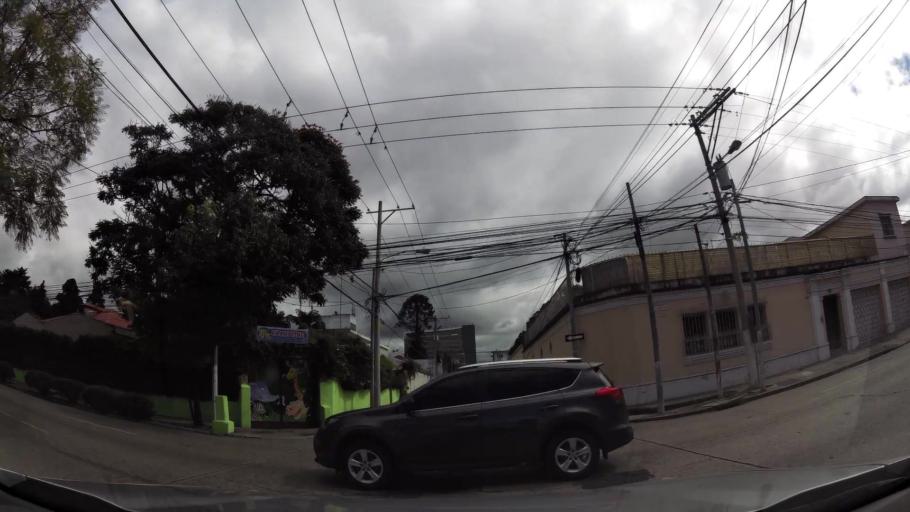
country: GT
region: Guatemala
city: Guatemala City
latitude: 14.6072
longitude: -90.5131
